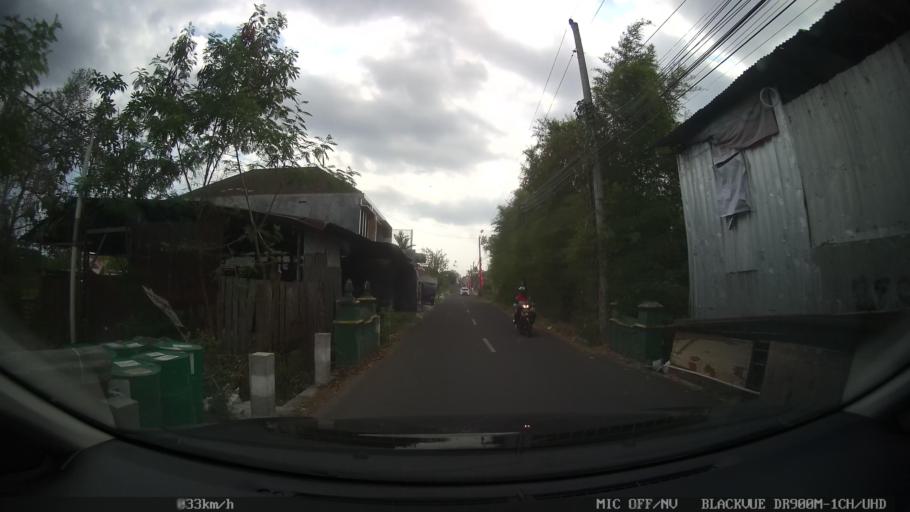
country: ID
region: Daerah Istimewa Yogyakarta
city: Yogyakarta
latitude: -7.7690
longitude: 110.3423
